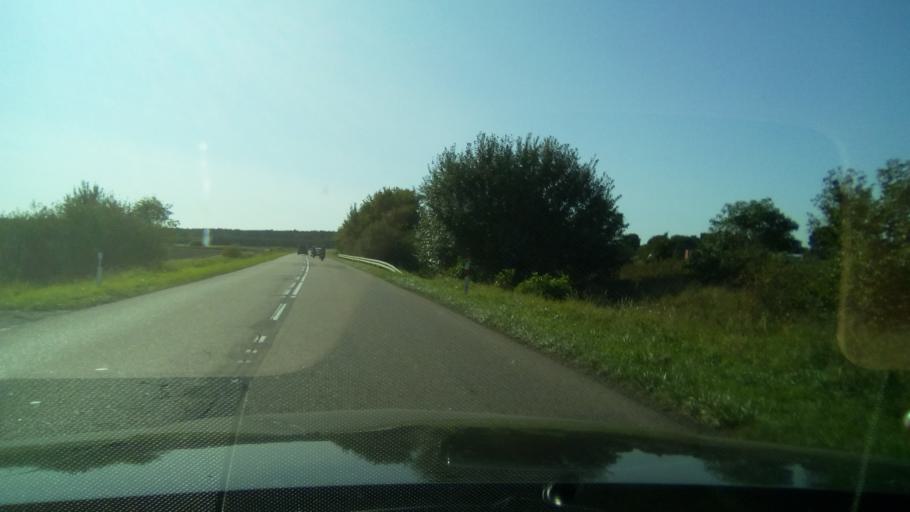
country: PL
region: West Pomeranian Voivodeship
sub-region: Powiat gryficki
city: Gryfice
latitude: 53.8140
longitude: 15.1336
